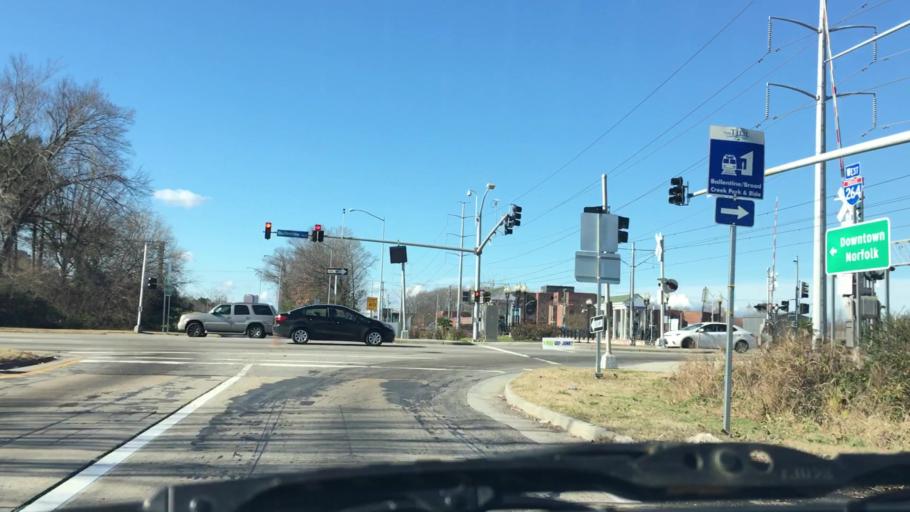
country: US
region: Virginia
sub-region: City of Norfolk
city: Norfolk
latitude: 36.8461
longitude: -76.2523
